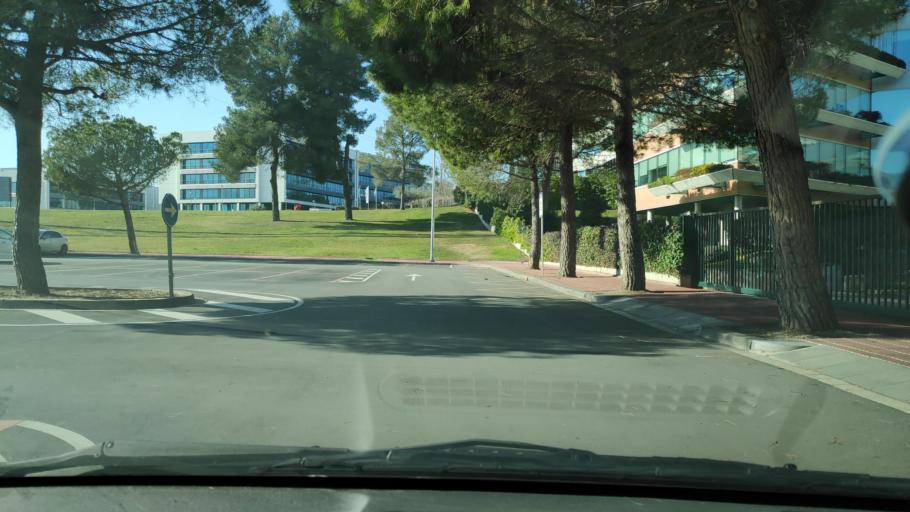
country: ES
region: Catalonia
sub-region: Provincia de Barcelona
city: Sant Cugat del Valles
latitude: 41.4919
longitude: 2.0780
